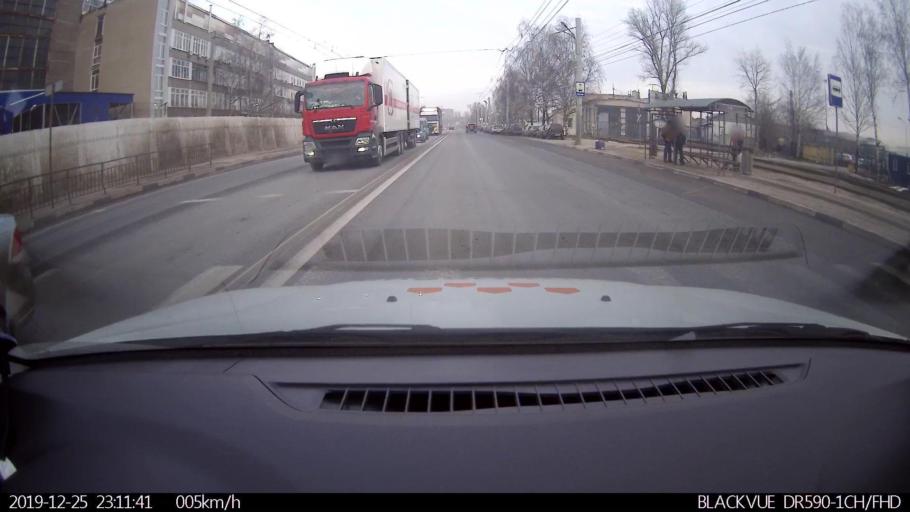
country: RU
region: Nizjnij Novgorod
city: Nizhniy Novgorod
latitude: 56.3202
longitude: 43.9069
